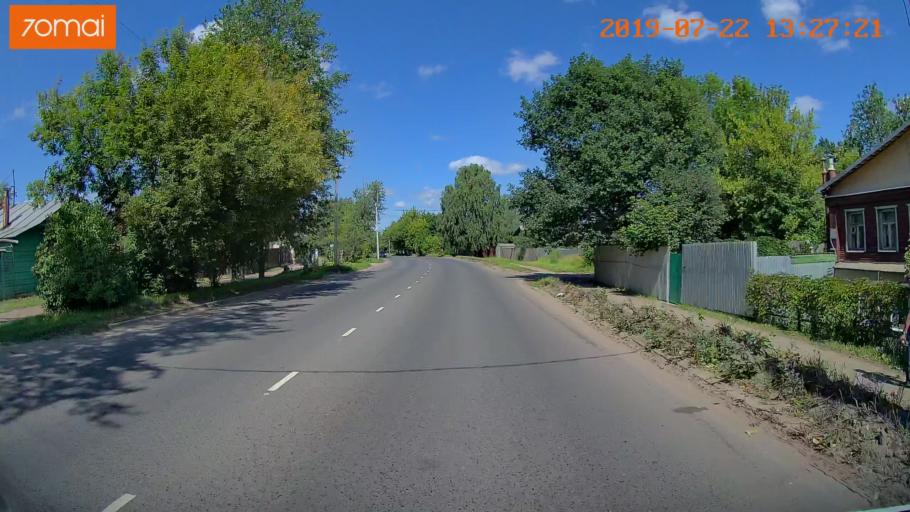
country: RU
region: Ivanovo
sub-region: Gorod Ivanovo
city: Ivanovo
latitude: 57.0340
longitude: 40.9496
